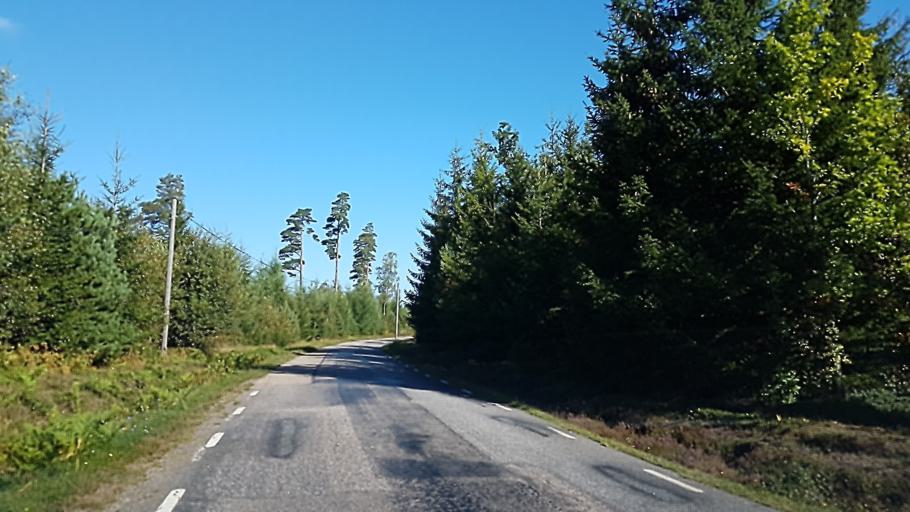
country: SE
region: Kronoberg
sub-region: Ljungby Kommun
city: Ljungby
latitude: 56.8069
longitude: 14.0327
